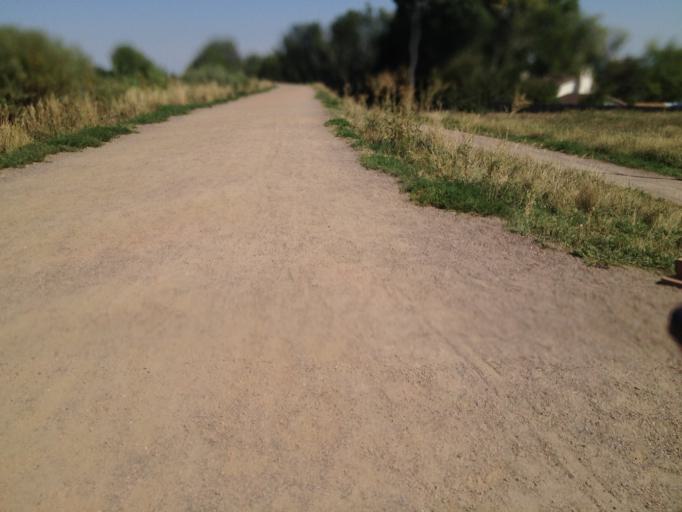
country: US
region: Colorado
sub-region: Boulder County
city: Lafayette
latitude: 39.9930
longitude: -105.1122
